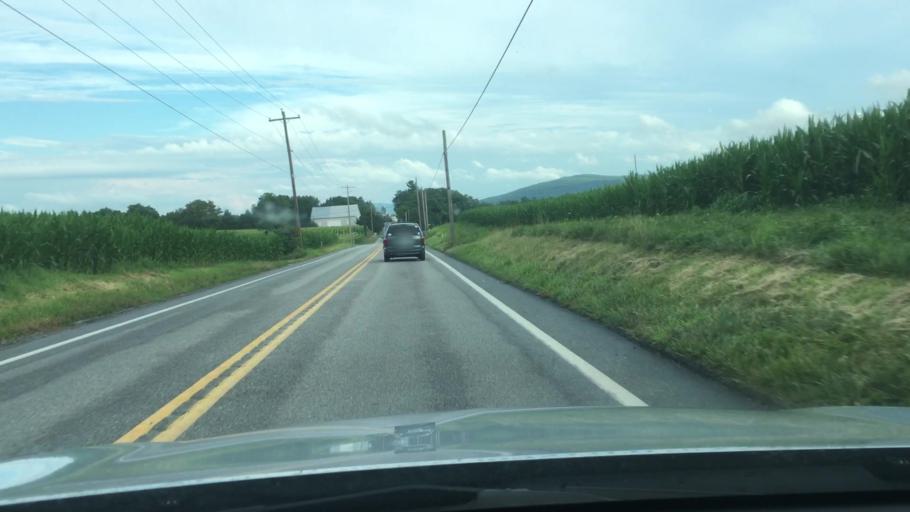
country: US
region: Pennsylvania
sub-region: Cumberland County
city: Boiling Springs
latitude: 40.1682
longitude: -77.1109
